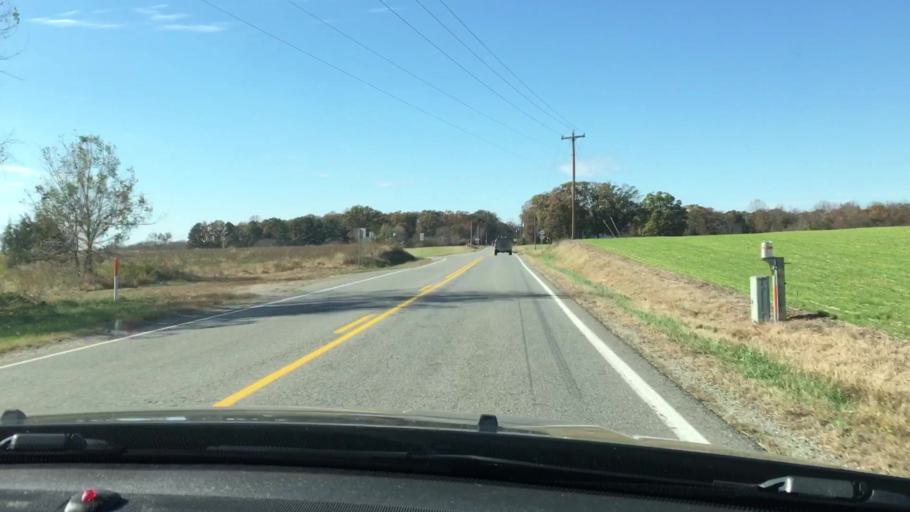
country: US
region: Virginia
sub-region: King William County
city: Central Garage
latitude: 37.7283
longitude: -77.1002
